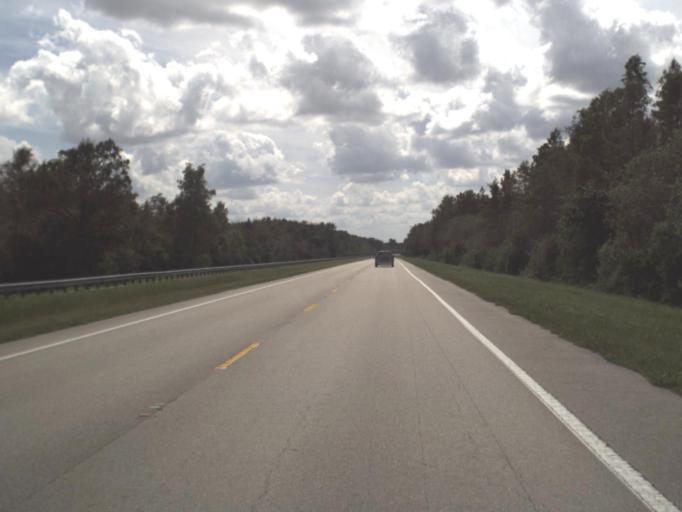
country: US
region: Florida
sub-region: Collier County
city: Orangetree
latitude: 26.0634
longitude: -81.3446
